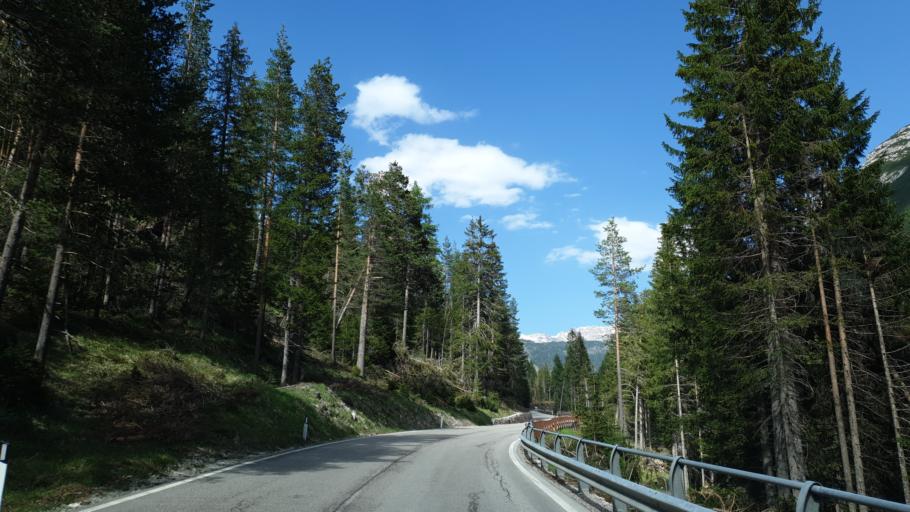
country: IT
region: Veneto
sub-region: Provincia di Belluno
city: Cortina d'Ampezzo
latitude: 46.6066
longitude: 12.1497
